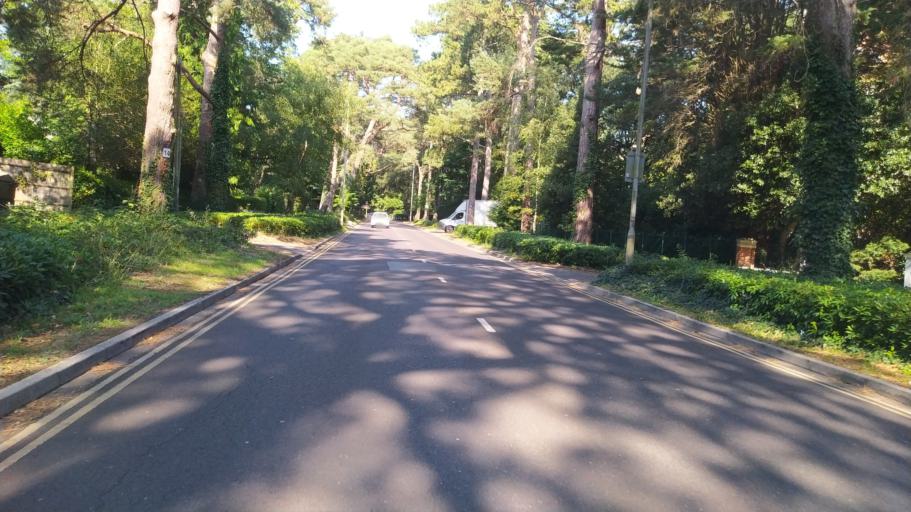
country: GB
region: England
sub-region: Bournemouth
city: Bournemouth
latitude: 50.7208
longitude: -1.9079
